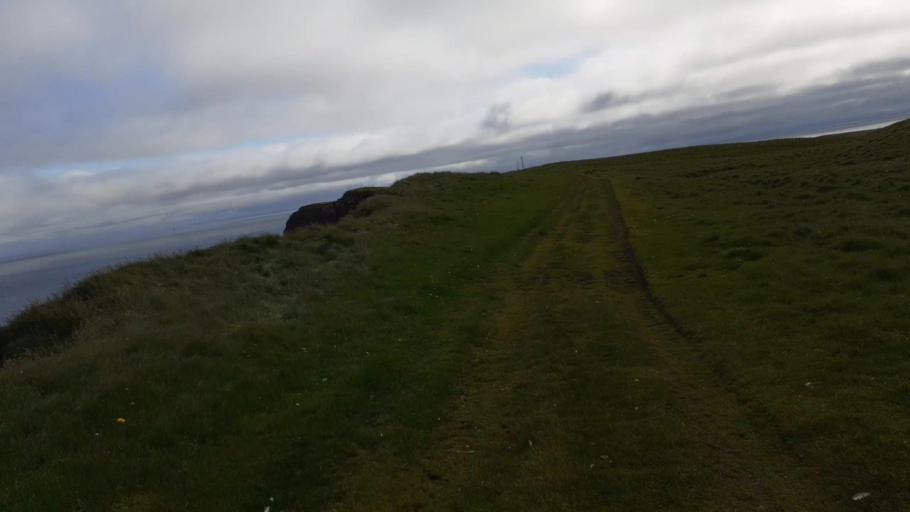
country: IS
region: Northeast
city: Dalvik
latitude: 66.5556
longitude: -18.0022
